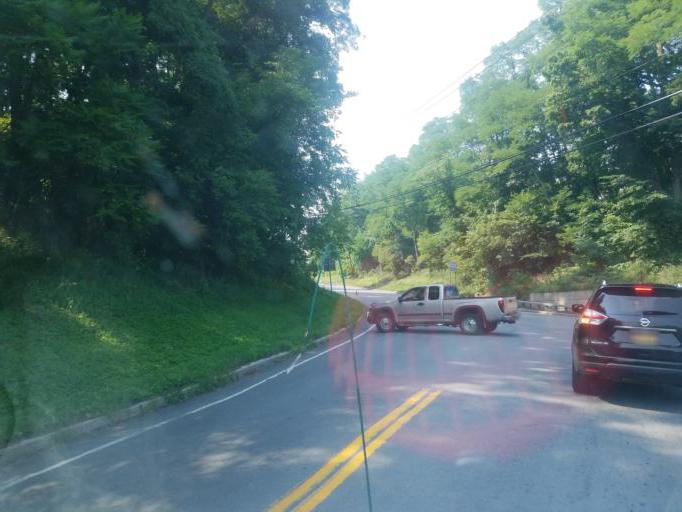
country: US
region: New York
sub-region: Montgomery County
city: Fonda
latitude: 42.9574
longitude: -74.3830
